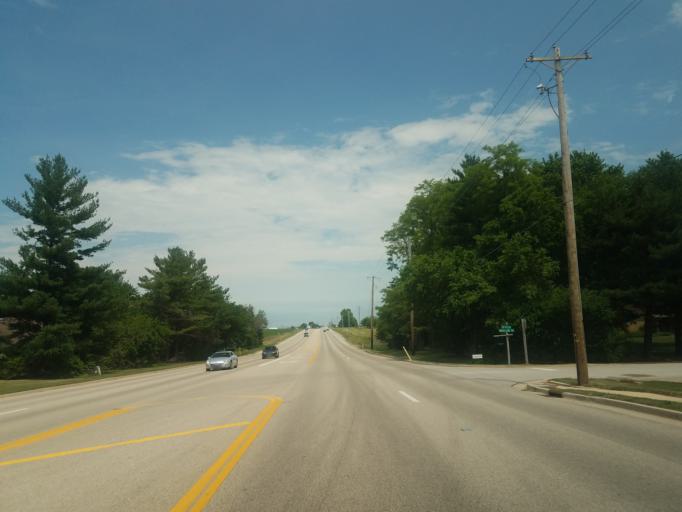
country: US
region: Illinois
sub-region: McLean County
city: Downs
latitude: 40.4245
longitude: -88.9014
